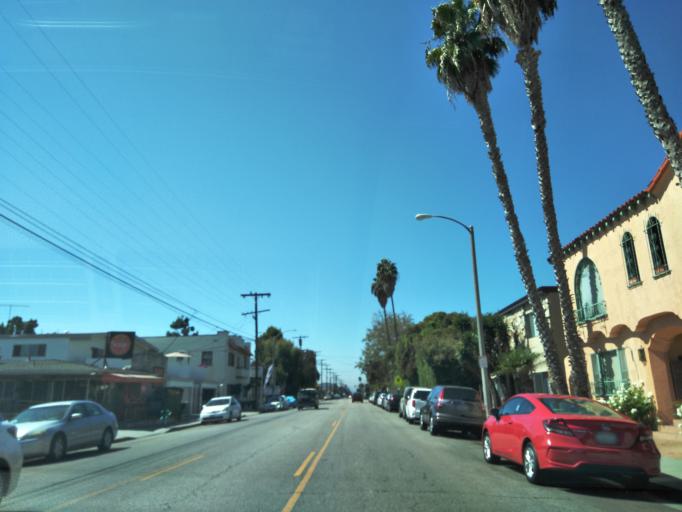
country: US
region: California
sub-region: Los Angeles County
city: Signal Hill
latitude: 33.7717
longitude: -118.1425
